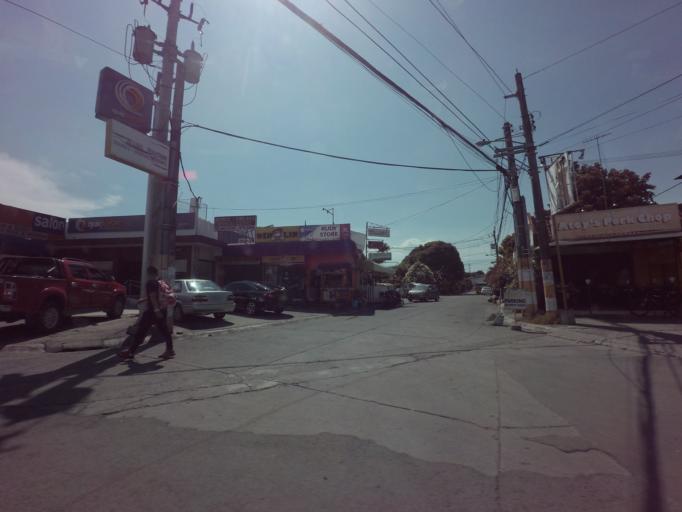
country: PH
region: Calabarzon
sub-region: Province of Rizal
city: Las Pinas
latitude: 14.4435
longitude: 120.9925
